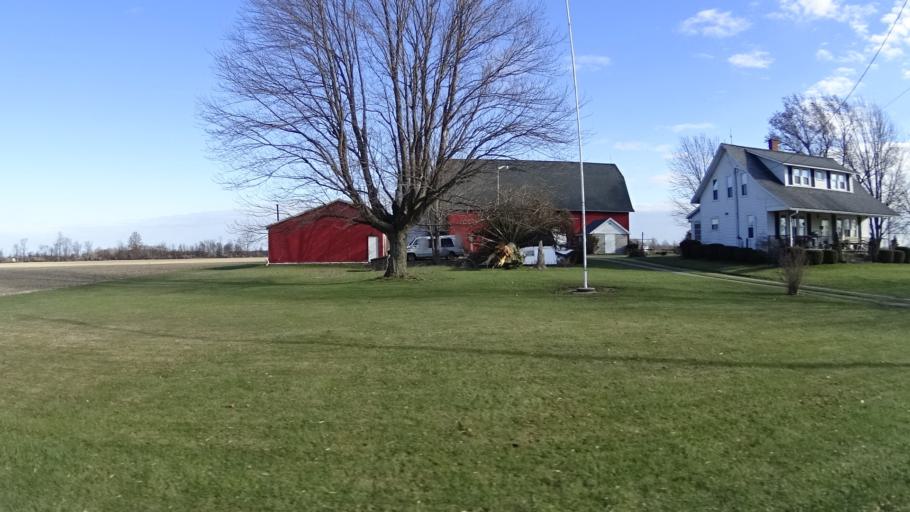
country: US
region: Ohio
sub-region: Lorain County
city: Camden
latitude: 41.2104
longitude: -82.3214
